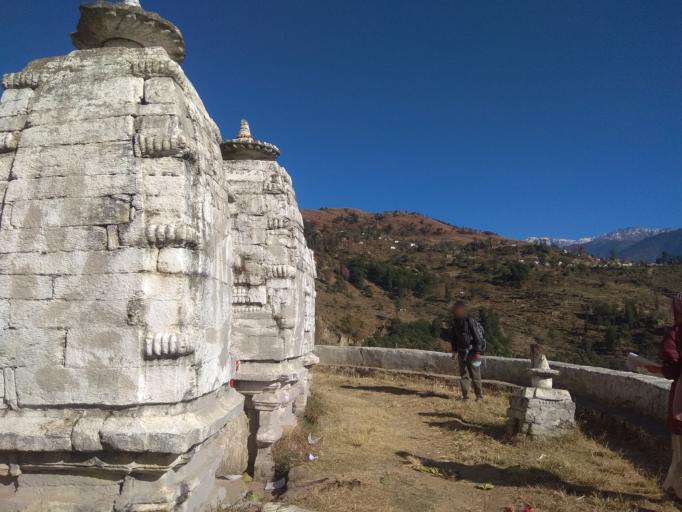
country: NP
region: Far Western
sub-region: Seti Zone
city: Achham
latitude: 29.2553
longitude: 81.6366
